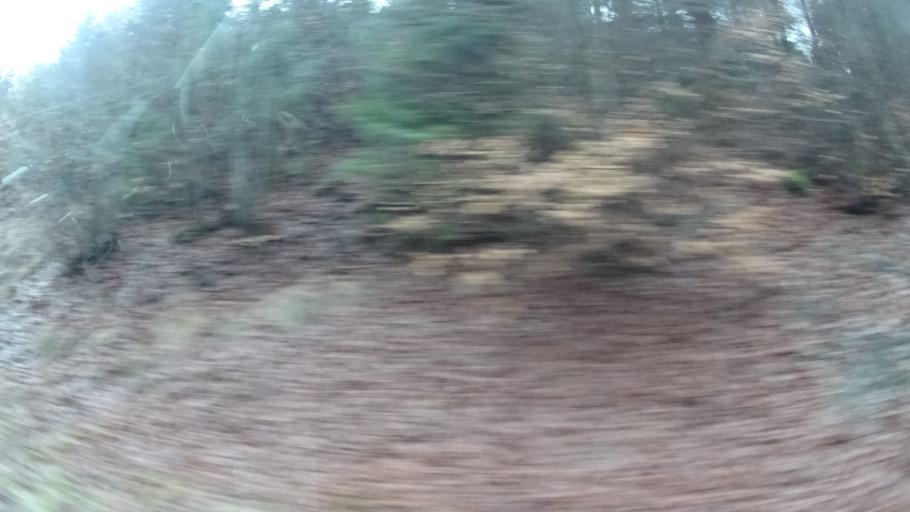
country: DE
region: Thuringia
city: Masserberg
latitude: 50.5359
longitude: 10.9711
